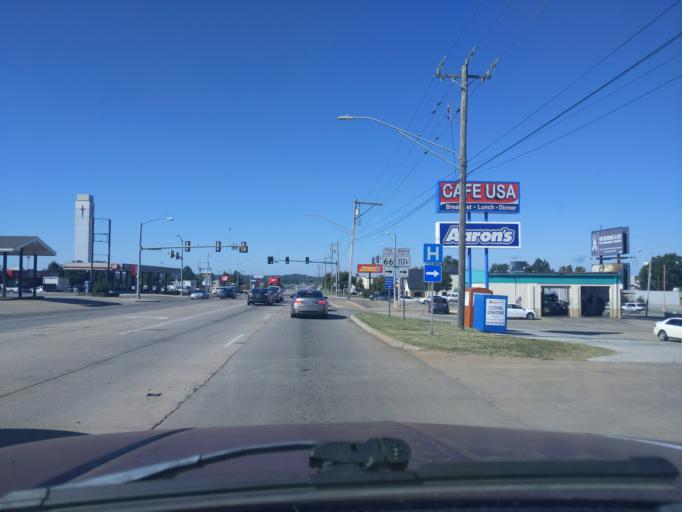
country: US
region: Oklahoma
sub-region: Creek County
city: Sapulpa
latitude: 35.9885
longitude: -96.0979
